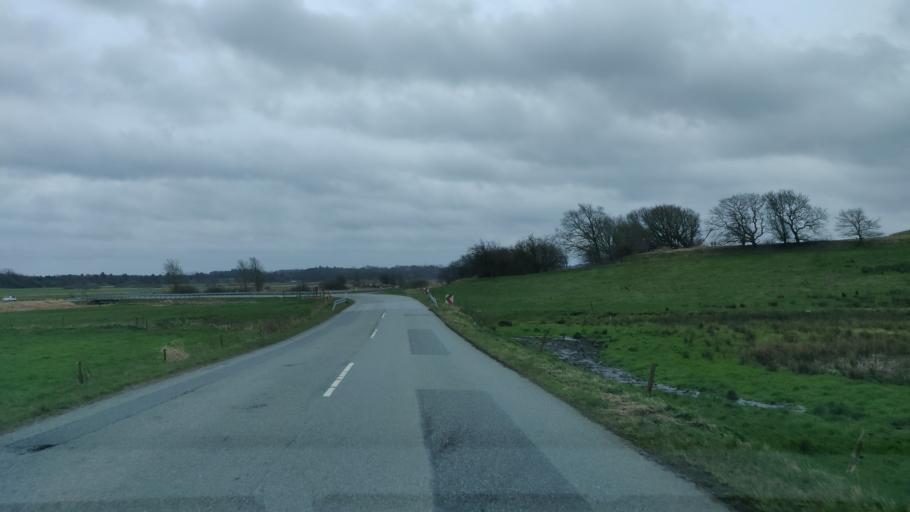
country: DK
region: Central Jutland
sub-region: Skive Kommune
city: Hojslev
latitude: 56.5718
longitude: 9.2370
